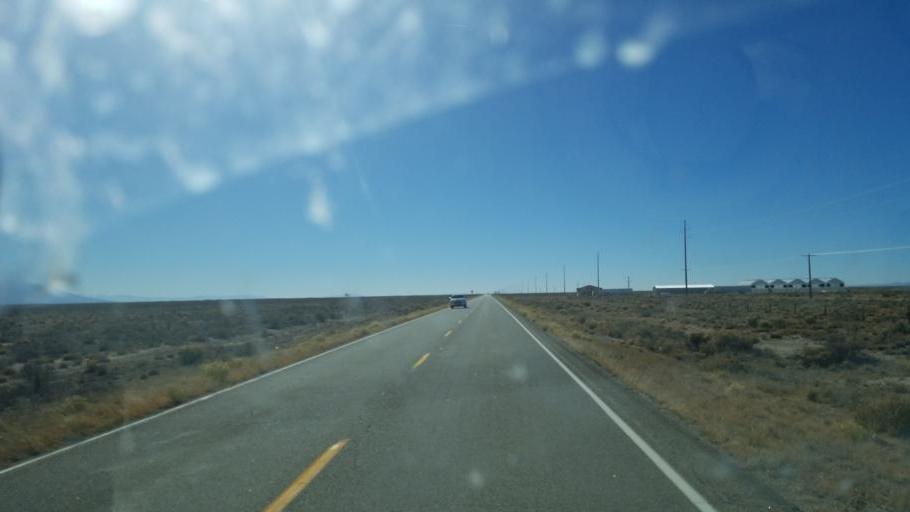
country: US
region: Colorado
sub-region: Saguache County
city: Saguache
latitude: 37.9526
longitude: -105.9034
